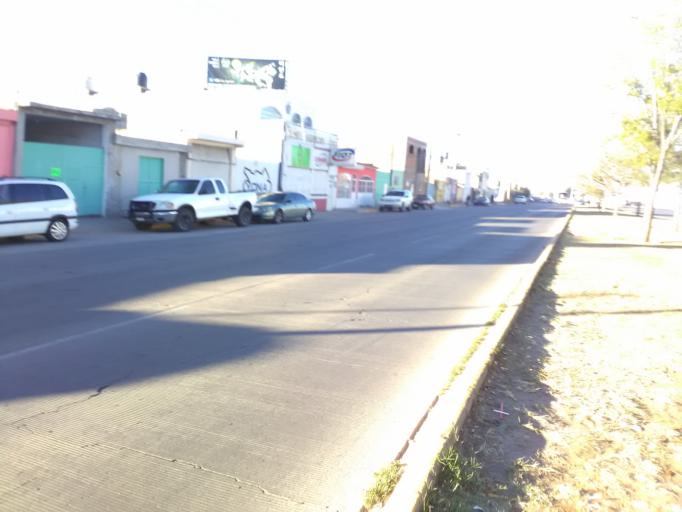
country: MX
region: Durango
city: Victoria de Durango
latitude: 24.0481
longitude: -104.6504
